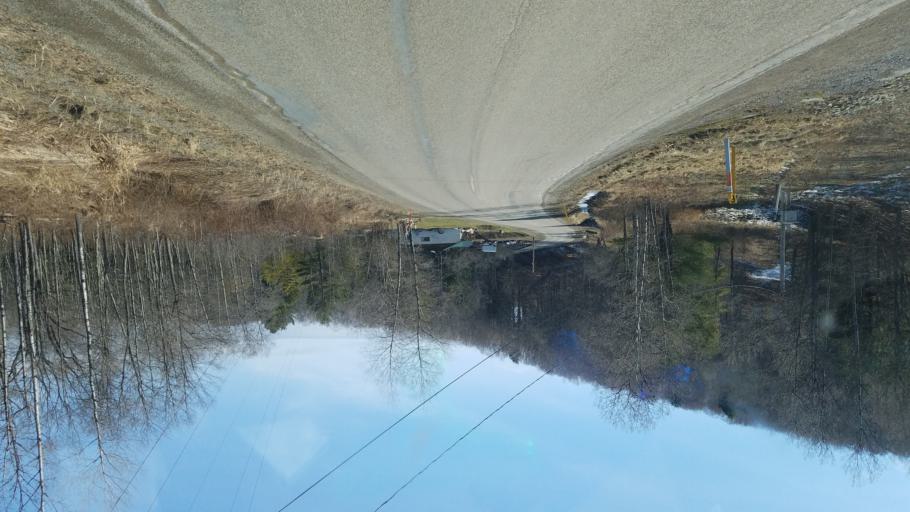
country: US
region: New York
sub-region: Allegany County
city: Andover
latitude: 41.9454
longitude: -77.8197
